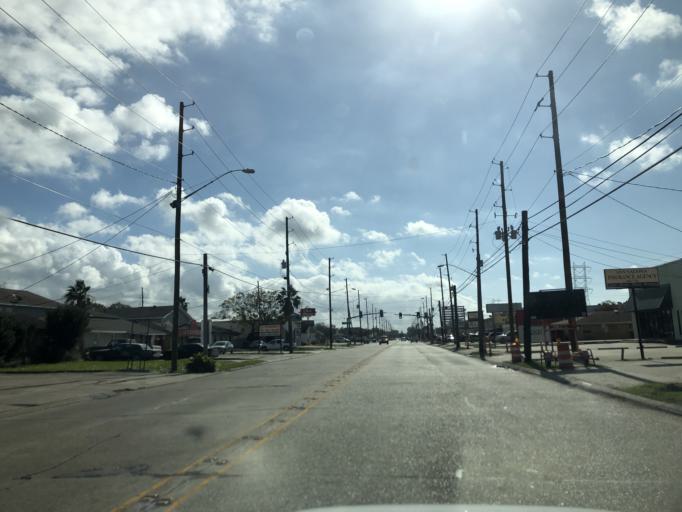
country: US
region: Louisiana
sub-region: Jefferson Parish
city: Kenner
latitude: 30.0028
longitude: -90.2200
